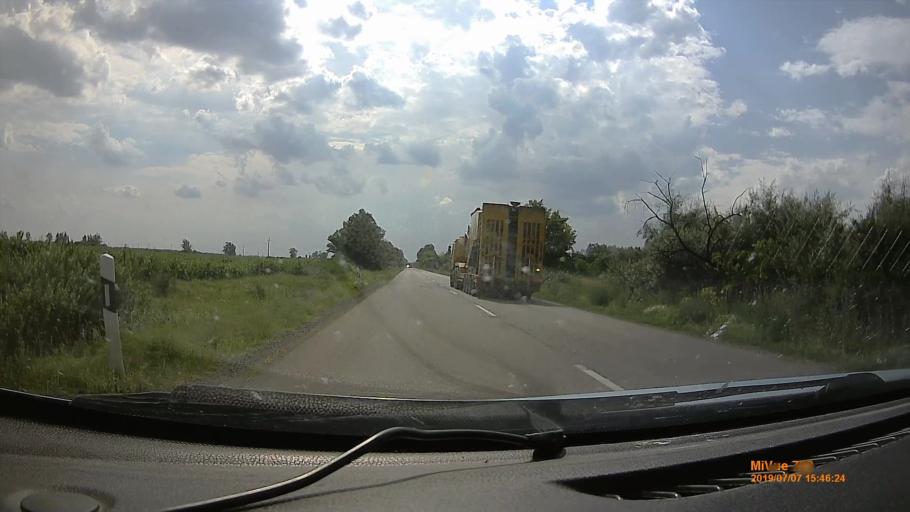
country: HU
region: Jasz-Nagykun-Szolnok
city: Jaszbereny
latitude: 47.5181
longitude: 19.8946
